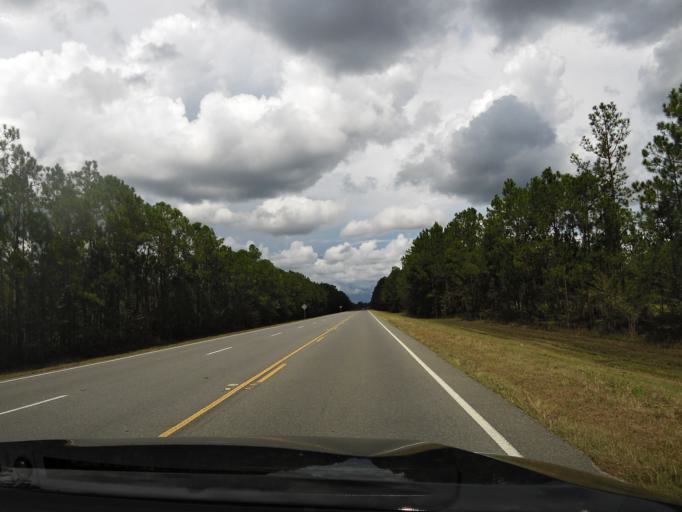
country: US
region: Georgia
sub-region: Brantley County
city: Nahunta
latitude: 31.1803
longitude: -81.9880
